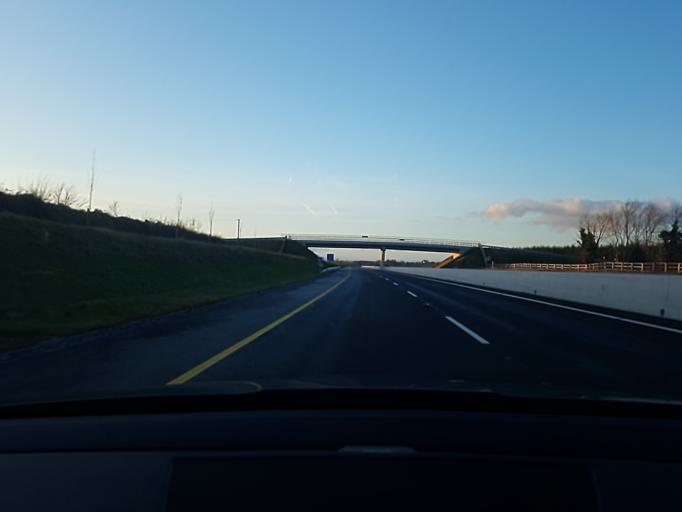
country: IE
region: Connaught
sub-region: County Galway
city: Tuam
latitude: 53.4903
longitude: -8.8683
